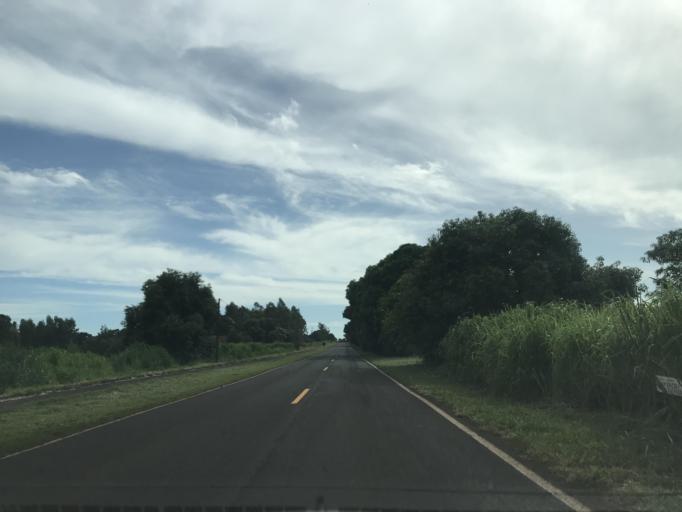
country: BR
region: Parana
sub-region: Terra Rica
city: Terra Rica
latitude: -22.7588
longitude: -52.6324
